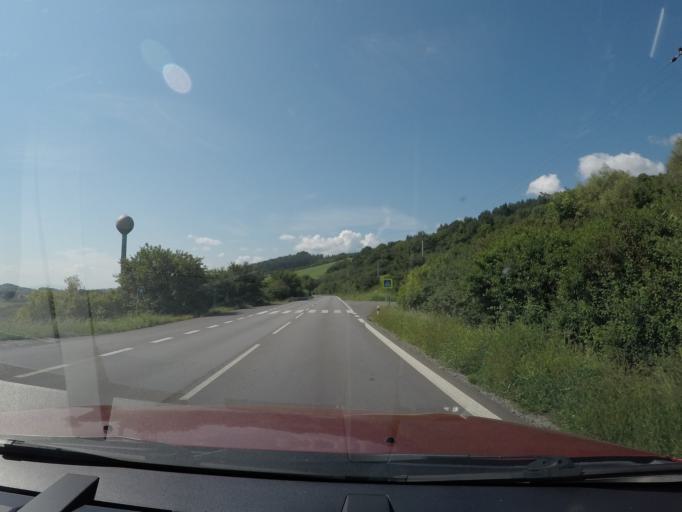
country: SK
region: Presovsky
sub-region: Okres Presov
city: Presov
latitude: 48.9180
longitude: 21.2403
